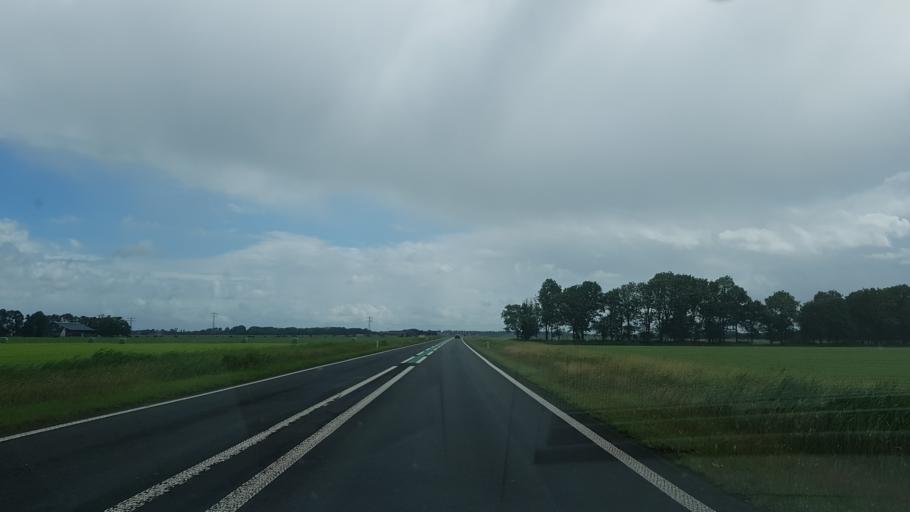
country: NL
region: Friesland
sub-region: Gemeente Dantumadiel
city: Rinsumageast
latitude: 53.3024
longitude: 5.9509
